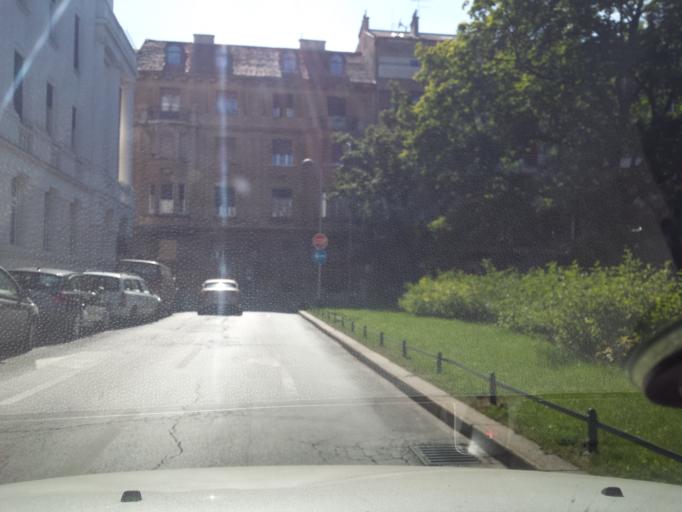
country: HR
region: Grad Zagreb
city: Zagreb - Centar
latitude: 45.8065
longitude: 15.9744
